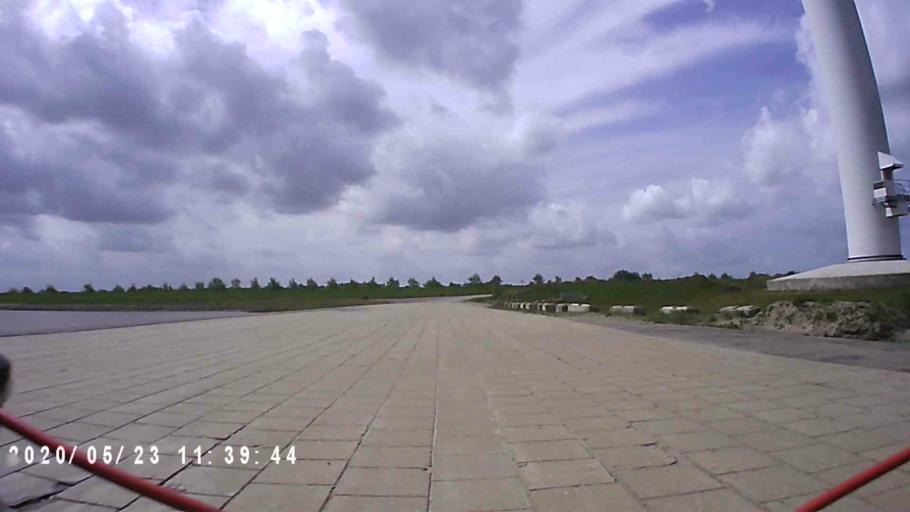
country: NL
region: Groningen
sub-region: Gemeente Delfzijl
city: Delfzijl
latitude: 53.3080
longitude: 7.0111
